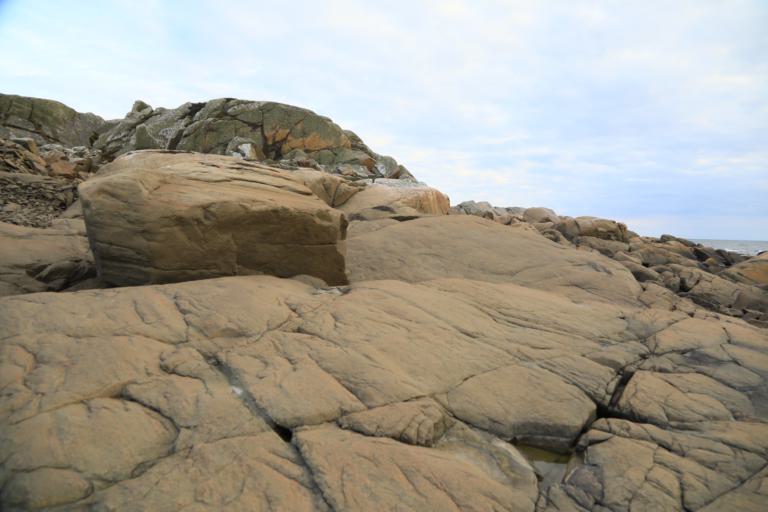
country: SE
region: Halland
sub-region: Varbergs Kommun
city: Traslovslage
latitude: 57.0651
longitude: 12.2428
